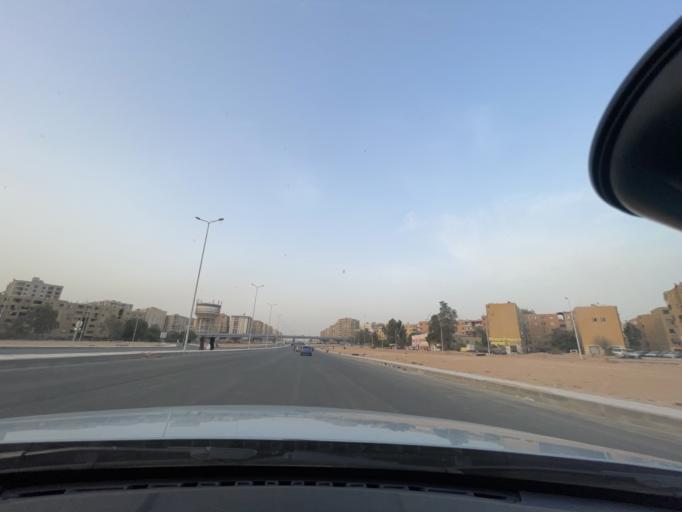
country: EG
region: Muhafazat al Qahirah
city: Cairo
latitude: 30.0450
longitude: 31.3636
